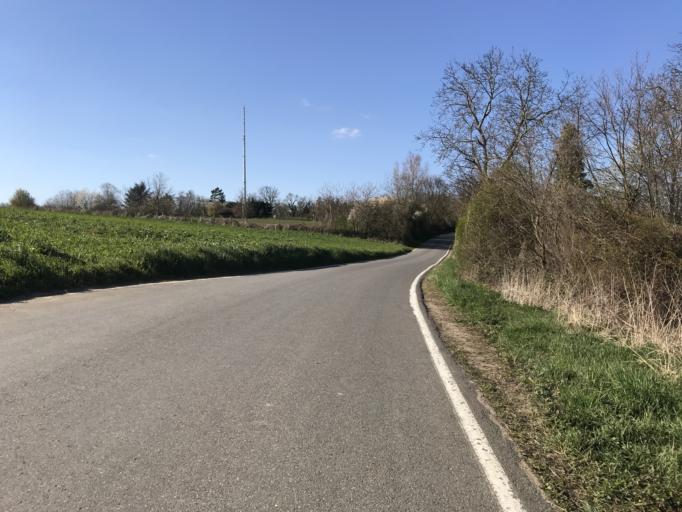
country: DE
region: Rheinland-Pfalz
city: Gau-Algesheim
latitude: 49.9567
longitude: 8.0373
